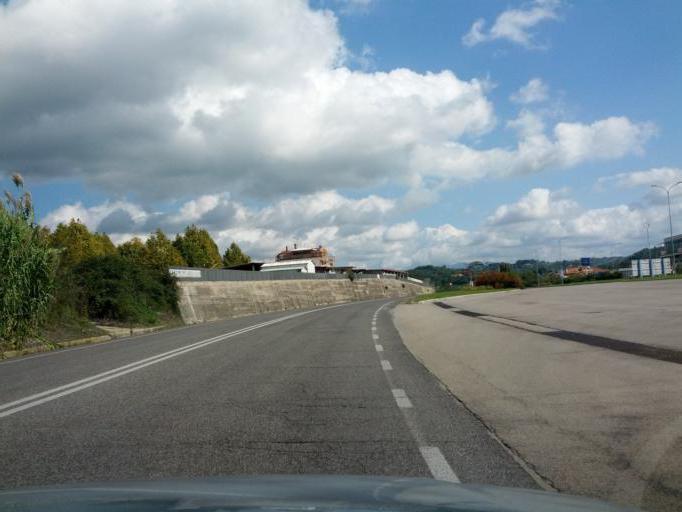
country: IT
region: Latium
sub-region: Provincia di Latina
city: Penitro
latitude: 41.2777
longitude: 13.7057
